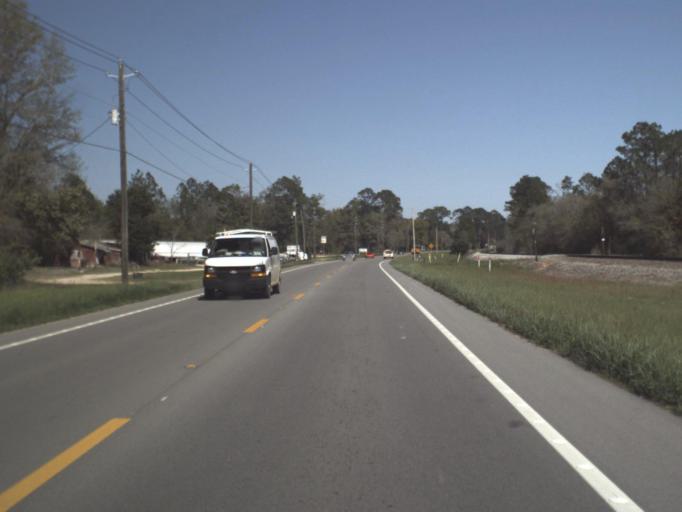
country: US
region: Florida
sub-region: Walton County
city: DeFuniak Springs
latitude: 30.7277
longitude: -86.0837
